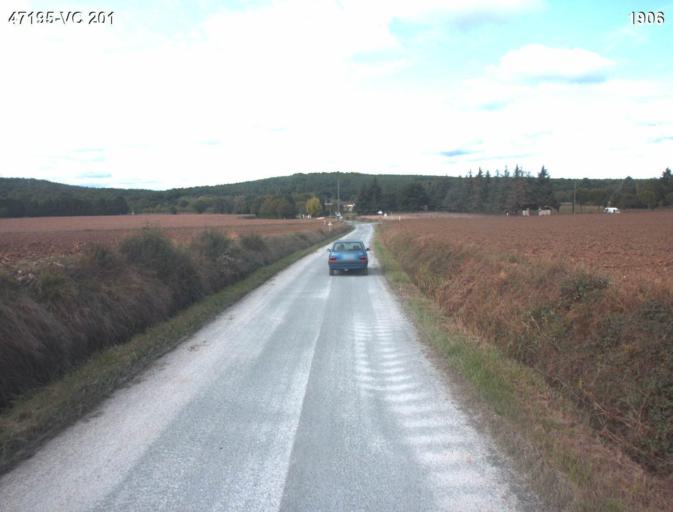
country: FR
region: Aquitaine
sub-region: Departement du Lot-et-Garonne
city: Barbaste
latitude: 44.1331
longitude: 0.2983
